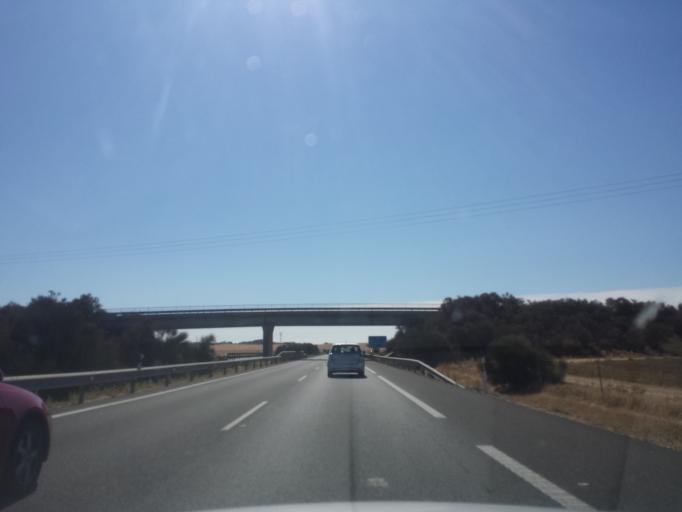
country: ES
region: Castille and Leon
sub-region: Provincia de Valladolid
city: Mota del Marques
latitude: 41.6258
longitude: -5.1729
